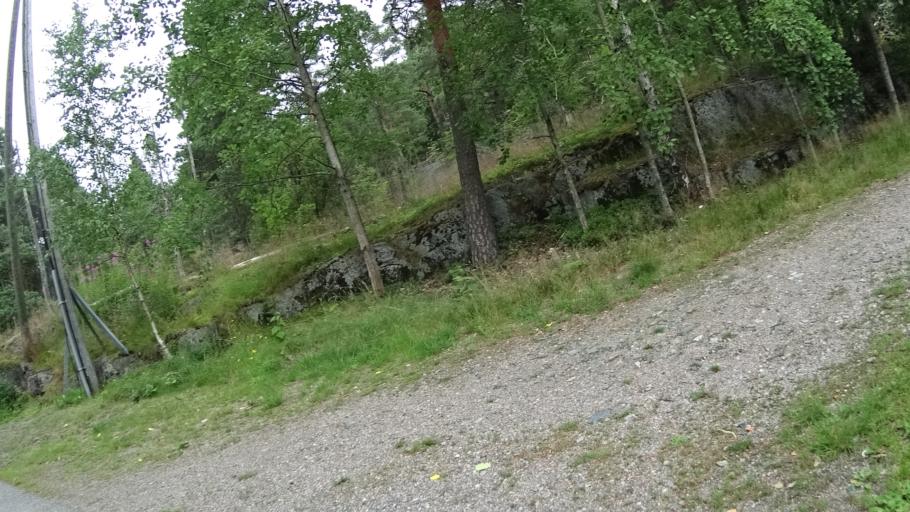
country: FI
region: Uusimaa
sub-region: Helsinki
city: Teekkarikylae
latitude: 60.2235
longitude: 24.8326
